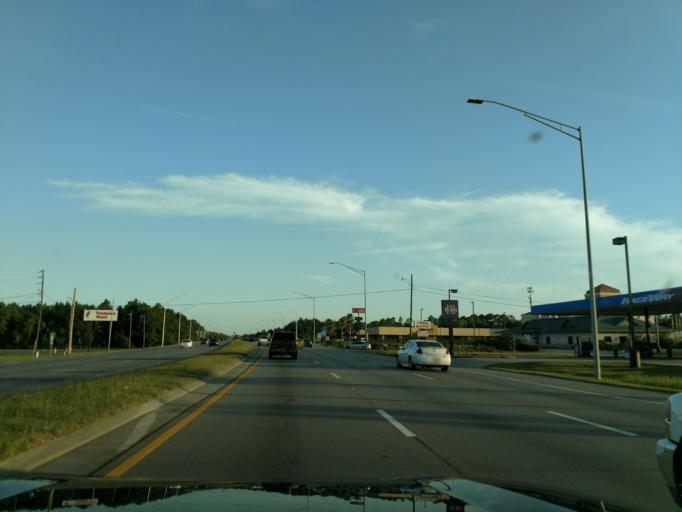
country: US
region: Mississippi
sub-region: Harrison County
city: West Gulfport
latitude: 30.4174
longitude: -89.0930
